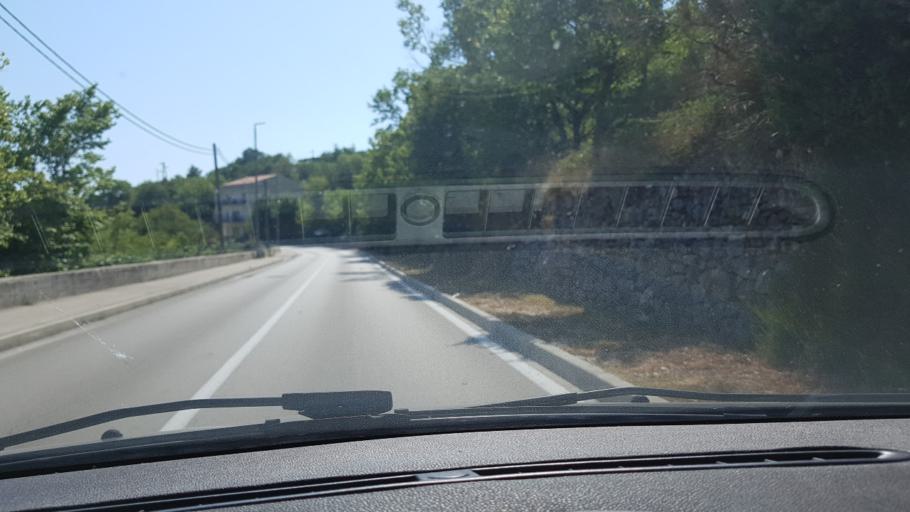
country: HR
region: Splitsko-Dalmatinska
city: Klis
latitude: 43.5639
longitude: 16.5254
